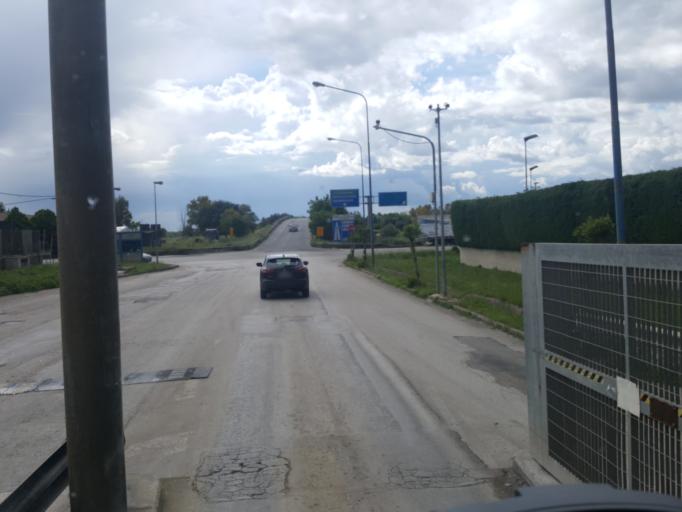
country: IT
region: Campania
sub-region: Provincia di Napoli
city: Pascarola
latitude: 40.9910
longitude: 14.2972
